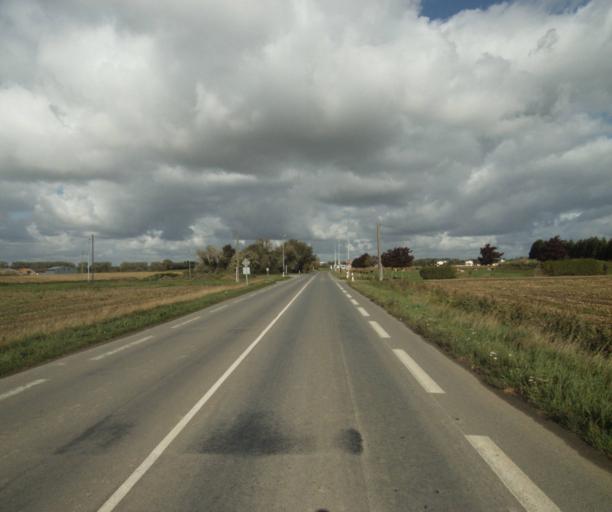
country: FR
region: Nord-Pas-de-Calais
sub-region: Departement du Nord
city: Frelinghien
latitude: 50.7187
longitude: 2.9394
